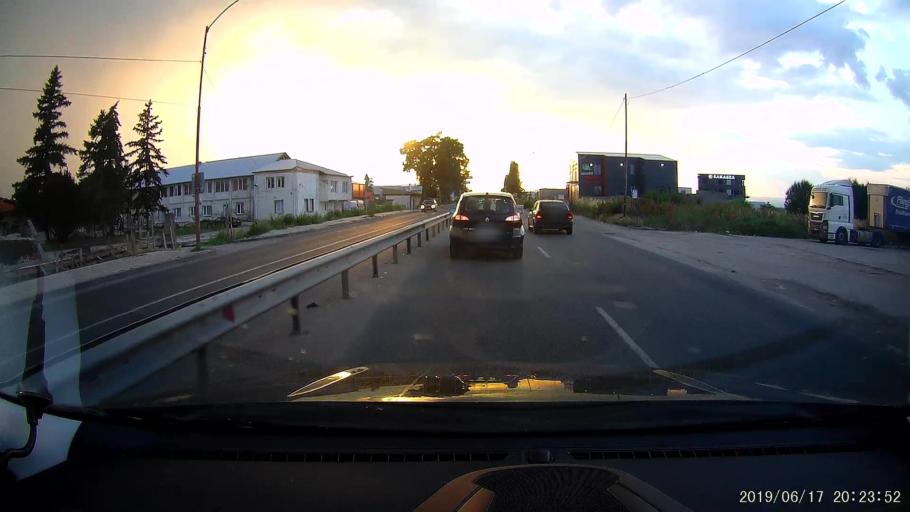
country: BG
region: Sofiya
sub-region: Obshtina Bozhurishte
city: Bozhurishte
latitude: 42.7374
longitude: 23.2433
